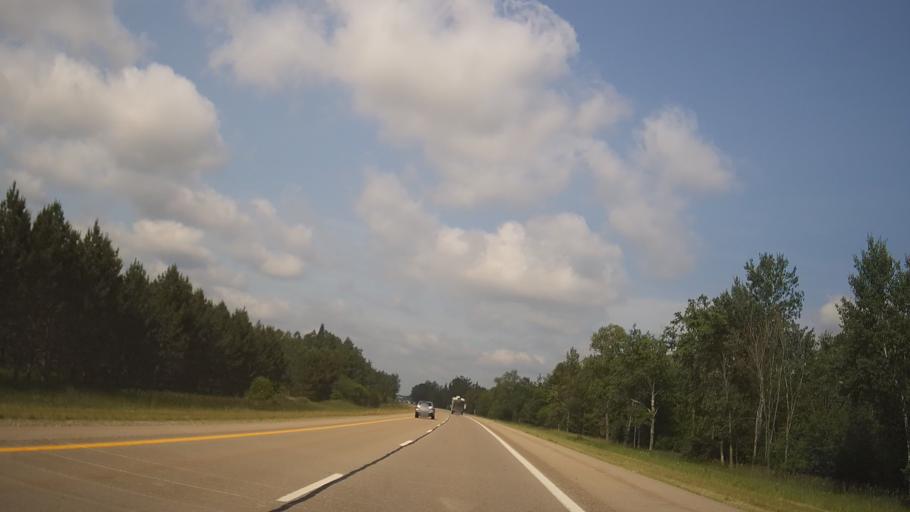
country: US
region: Michigan
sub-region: Roscommon County
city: Saint Helen
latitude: 44.3168
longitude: -84.4573
